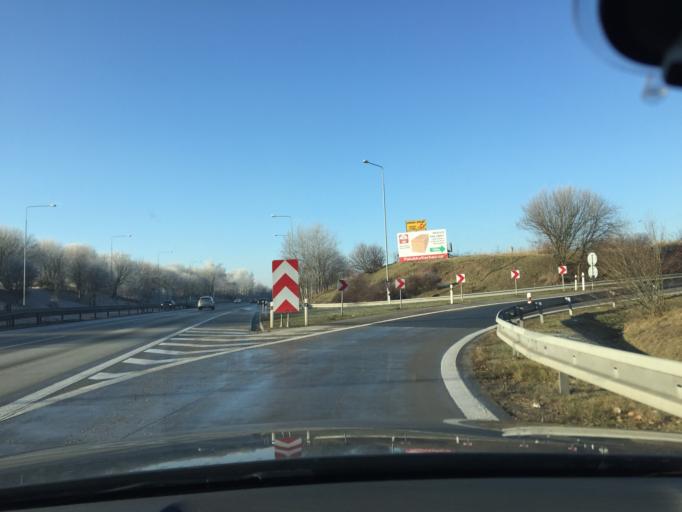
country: CZ
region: Central Bohemia
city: Trebotov
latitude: 50.0253
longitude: 14.2973
